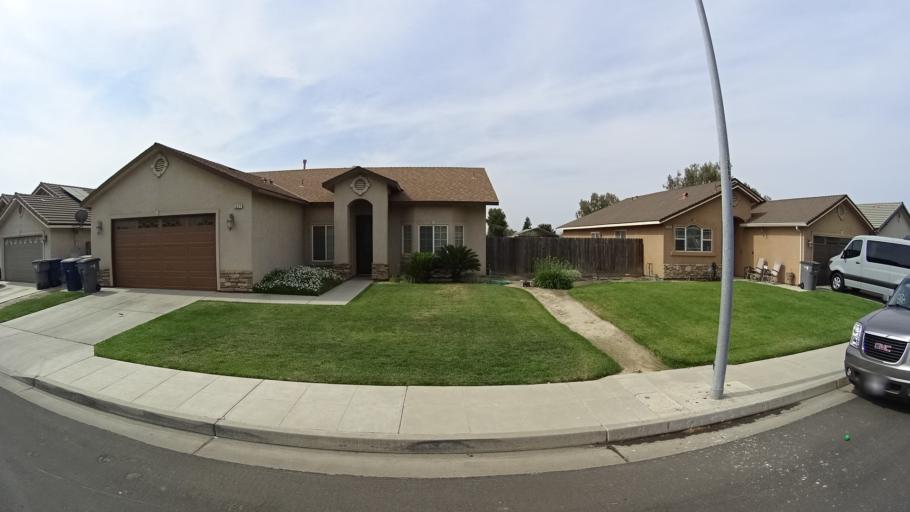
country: US
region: California
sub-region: Fresno County
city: West Park
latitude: 36.7667
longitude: -119.8929
